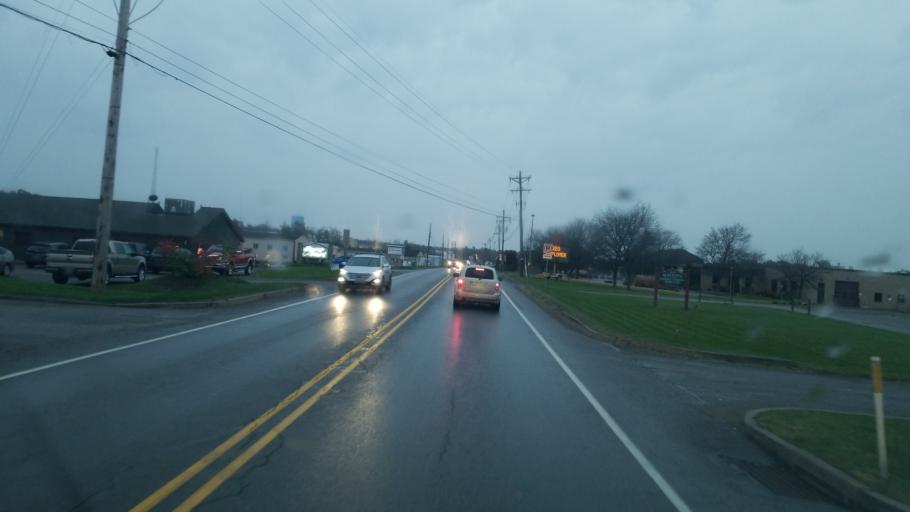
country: US
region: Pennsylvania
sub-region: Clarion County
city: Marianne
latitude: 41.2407
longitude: -79.4277
